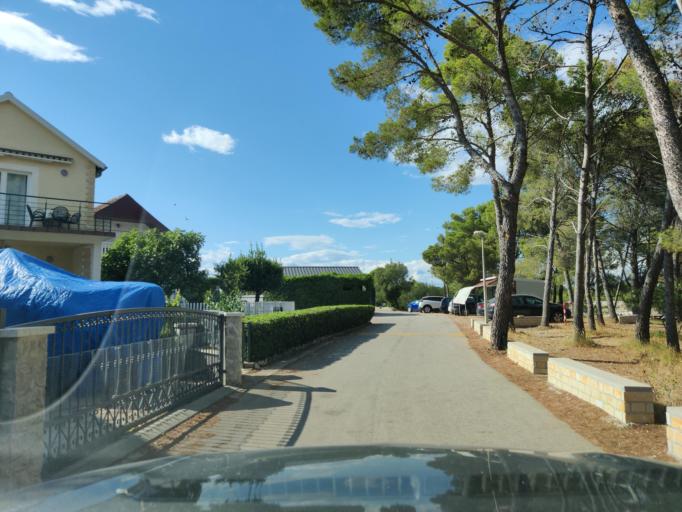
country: HR
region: Sibensko-Kniniska
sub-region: Grad Sibenik
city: Sibenik
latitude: 43.7264
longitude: 15.8469
